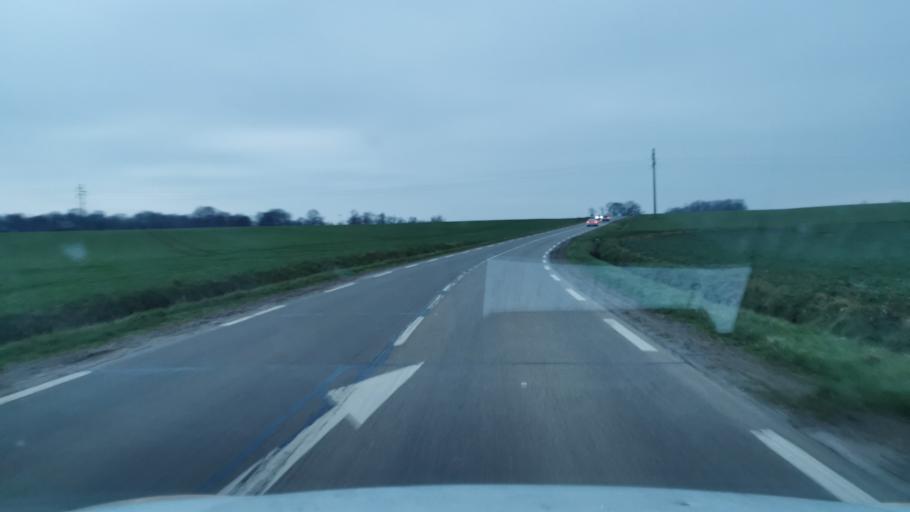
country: FR
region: Ile-de-France
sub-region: Departement des Yvelines
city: Longnes
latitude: 48.9339
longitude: 1.6272
